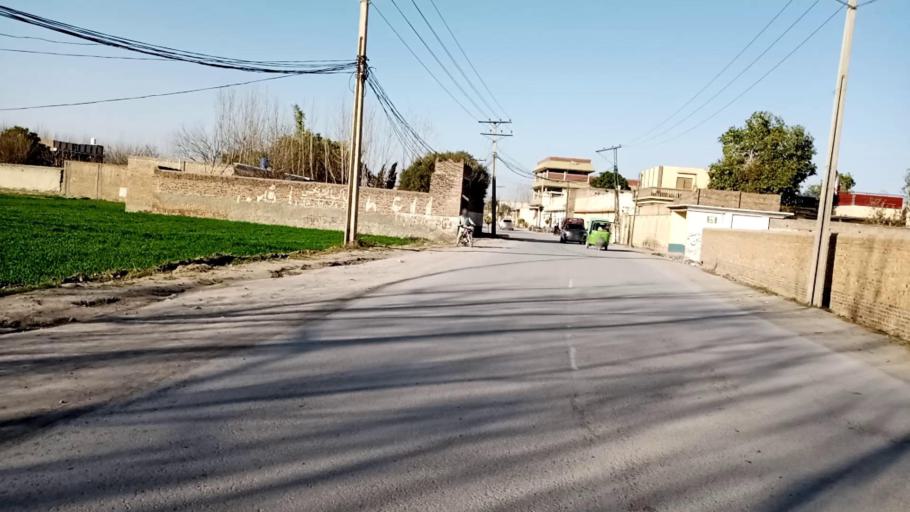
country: PK
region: Khyber Pakhtunkhwa
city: Peshawar
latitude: 34.0682
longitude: 71.5382
